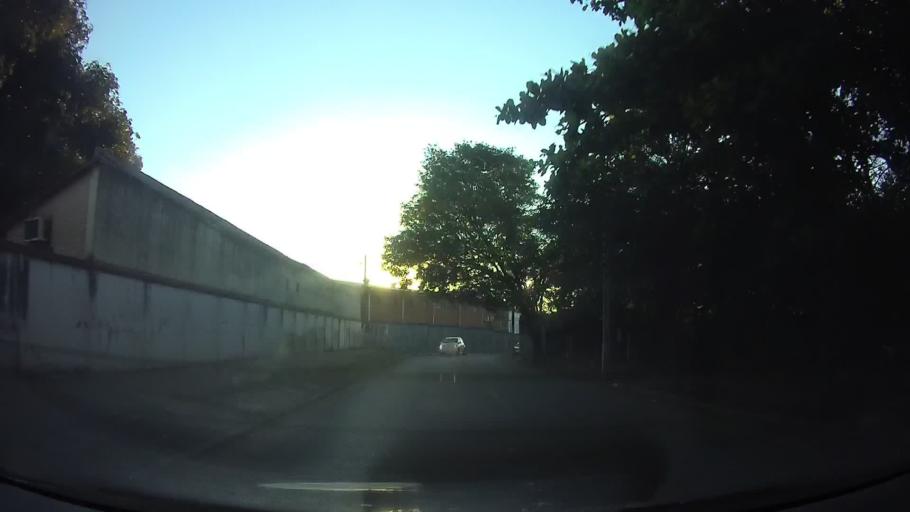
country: PY
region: Central
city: Fernando de la Mora
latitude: -25.3211
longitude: -57.5546
